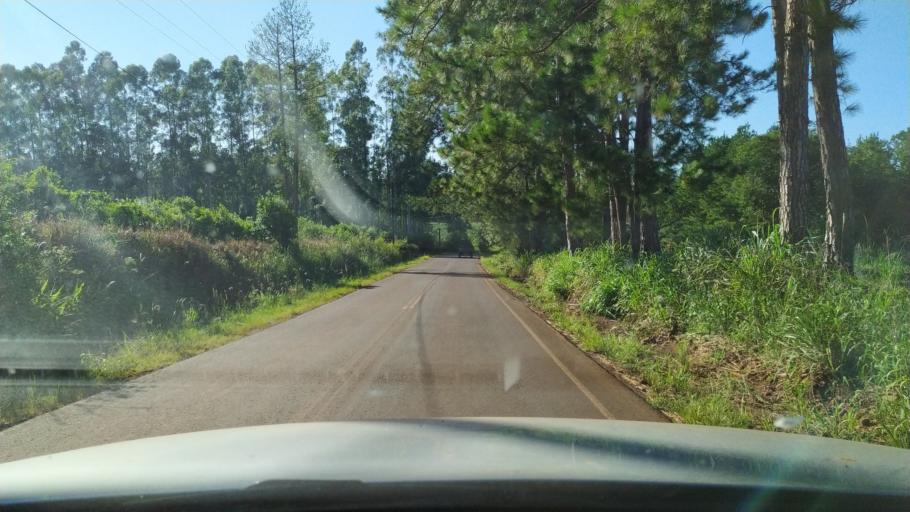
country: AR
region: Misiones
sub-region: Departamento de Montecarlo
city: Montecarlo
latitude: -26.5958
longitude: -54.7057
